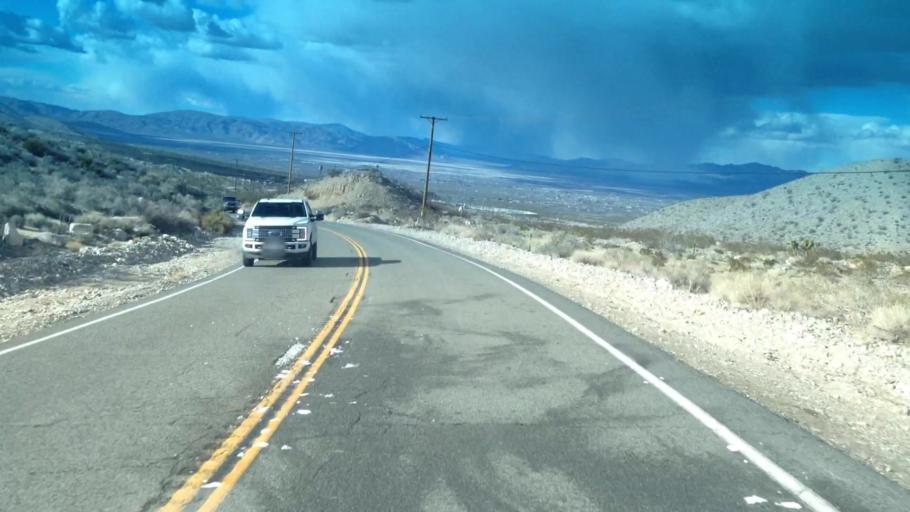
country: US
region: California
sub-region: San Bernardino County
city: Big Bear City
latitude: 34.3620
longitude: -116.8557
